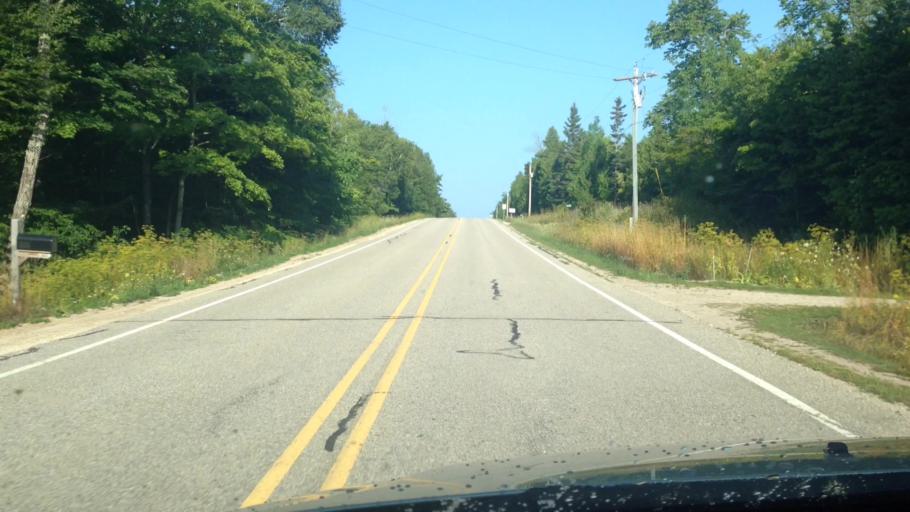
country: US
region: Michigan
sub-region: Mackinac County
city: Saint Ignace
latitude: 45.8939
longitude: -84.8118
